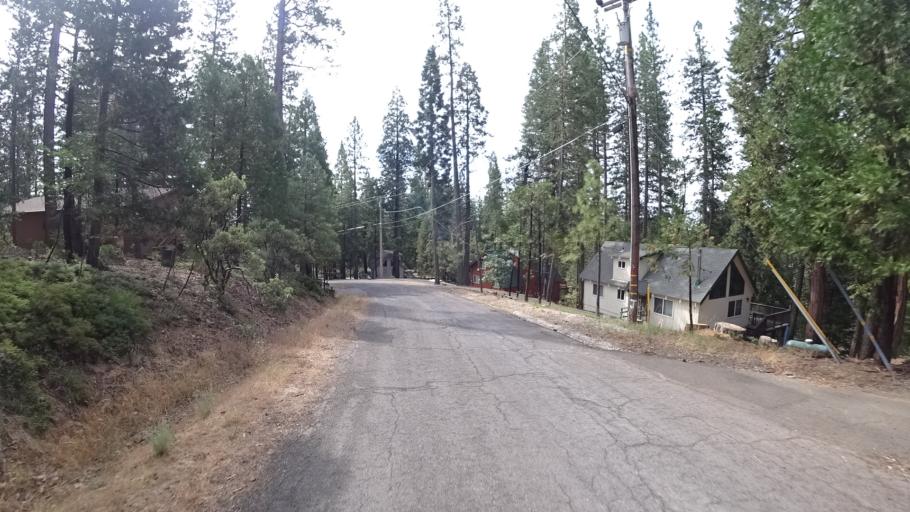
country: US
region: California
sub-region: Calaveras County
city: Arnold
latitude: 38.2483
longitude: -120.3457
